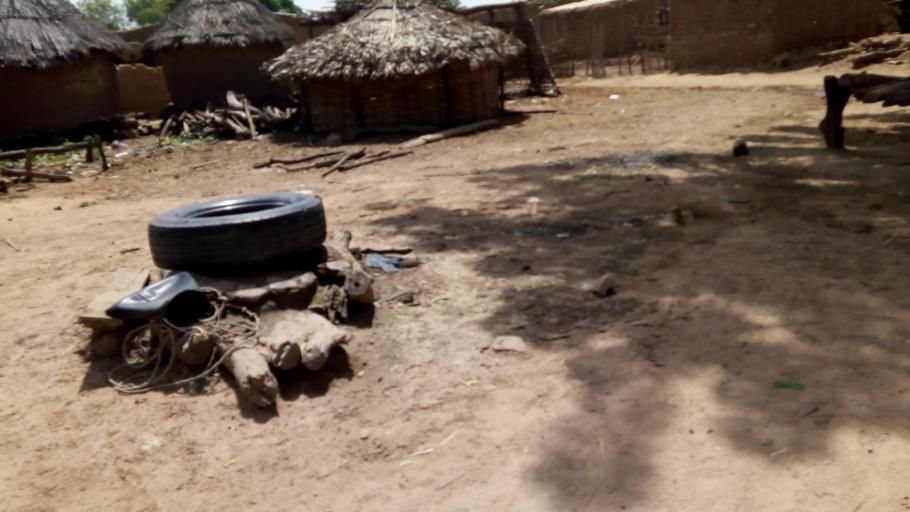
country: ML
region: Kayes
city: Kita
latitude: 13.4003
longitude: -8.8599
